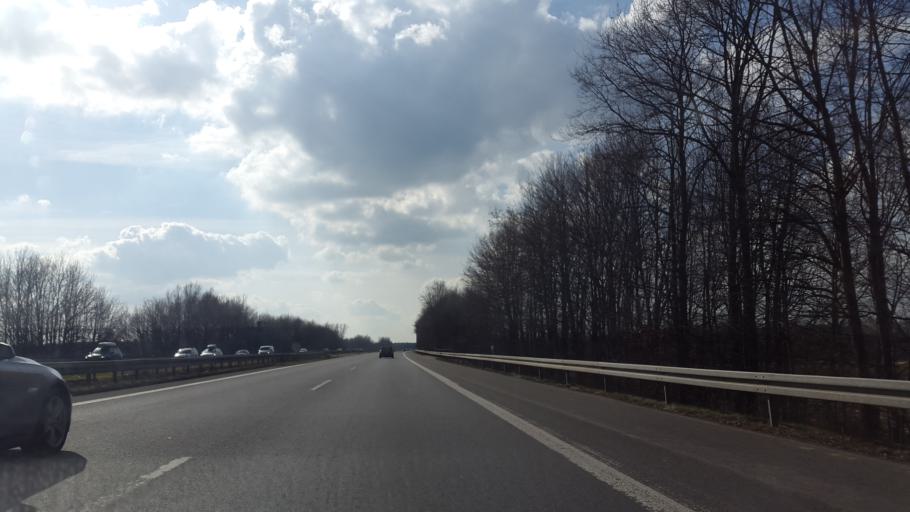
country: DE
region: Bavaria
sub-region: Regierungsbezirk Unterfranken
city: Kleinostheim
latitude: 50.0186
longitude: 9.0434
